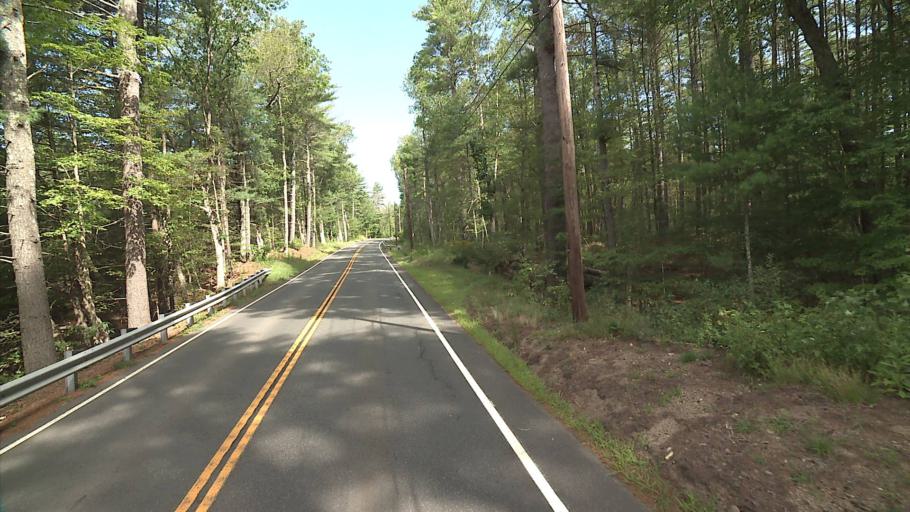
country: US
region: Connecticut
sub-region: Tolland County
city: Stafford
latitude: 42.0187
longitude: -72.3176
